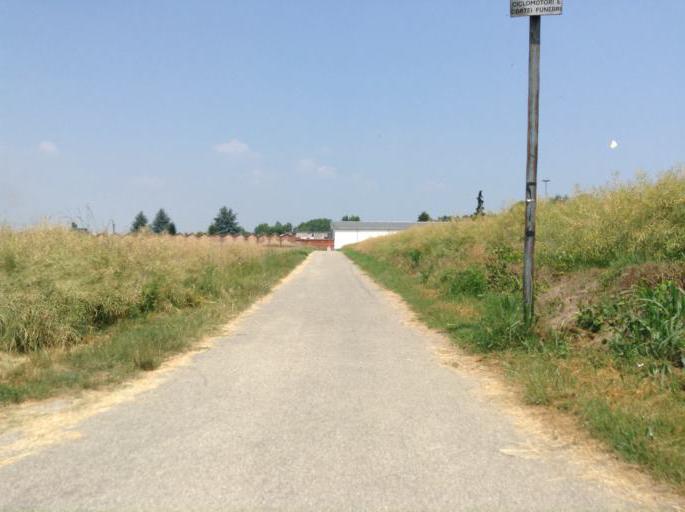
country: IT
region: Piedmont
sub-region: Provincia di Torino
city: Carignano
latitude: 44.9156
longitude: 7.6732
